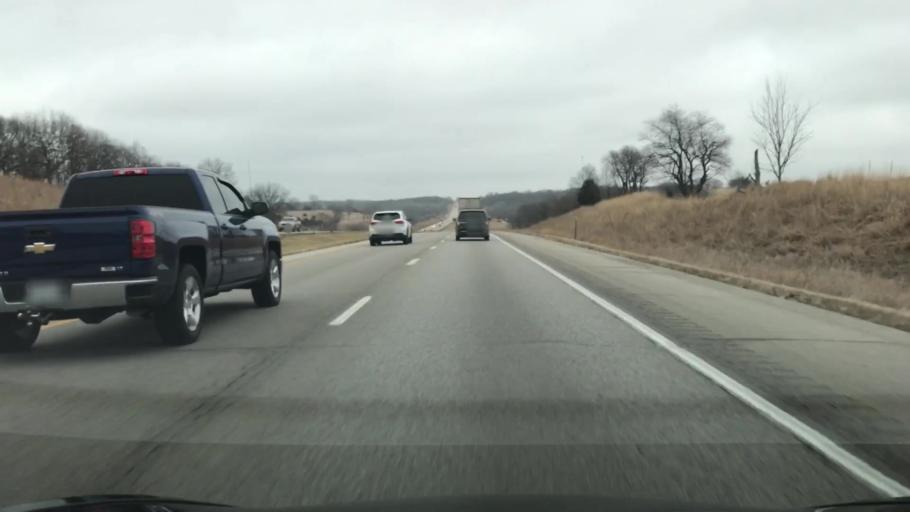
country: US
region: Iowa
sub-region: Madison County
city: Earlham
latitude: 41.5177
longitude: -94.1576
